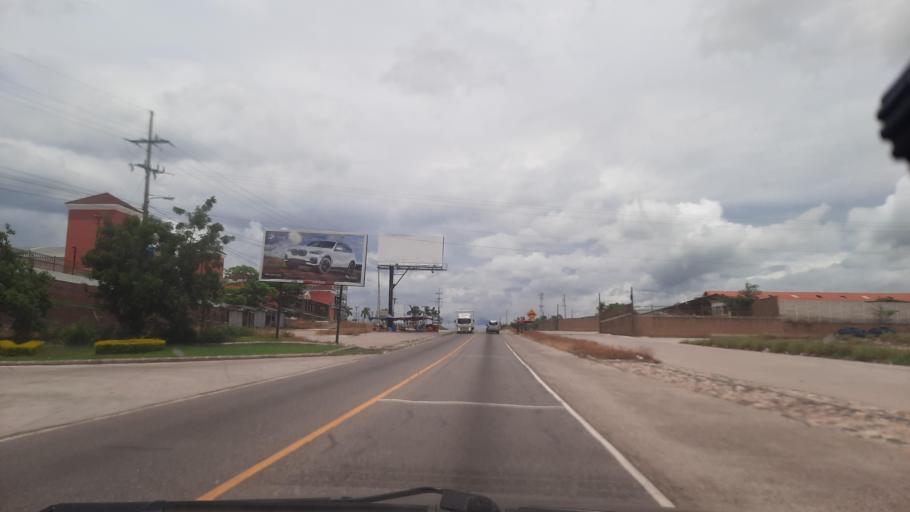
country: GT
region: Zacapa
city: Estanzuela
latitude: 15.0072
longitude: -89.5730
